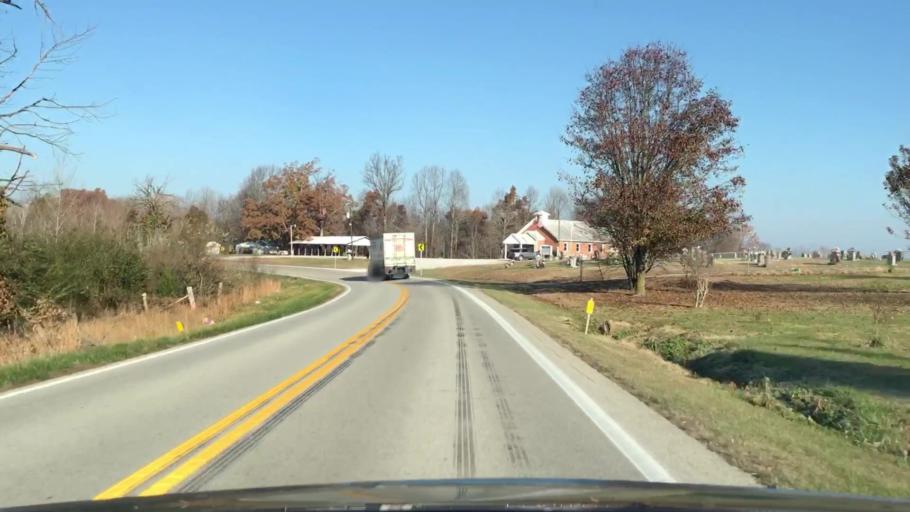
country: US
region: Kentucky
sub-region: Grayson County
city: Leitchfield
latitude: 37.3703
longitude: -86.2448
